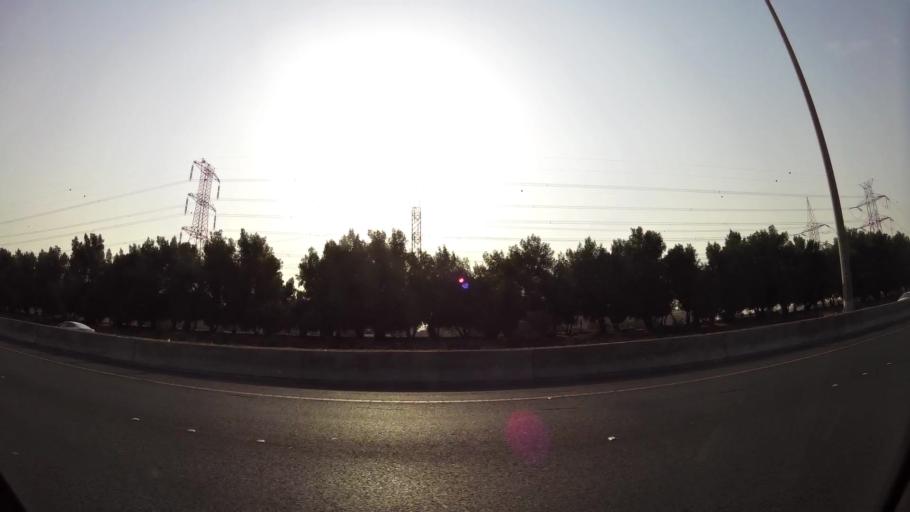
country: KW
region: Mubarak al Kabir
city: Sabah as Salim
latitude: 29.2764
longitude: 48.0369
